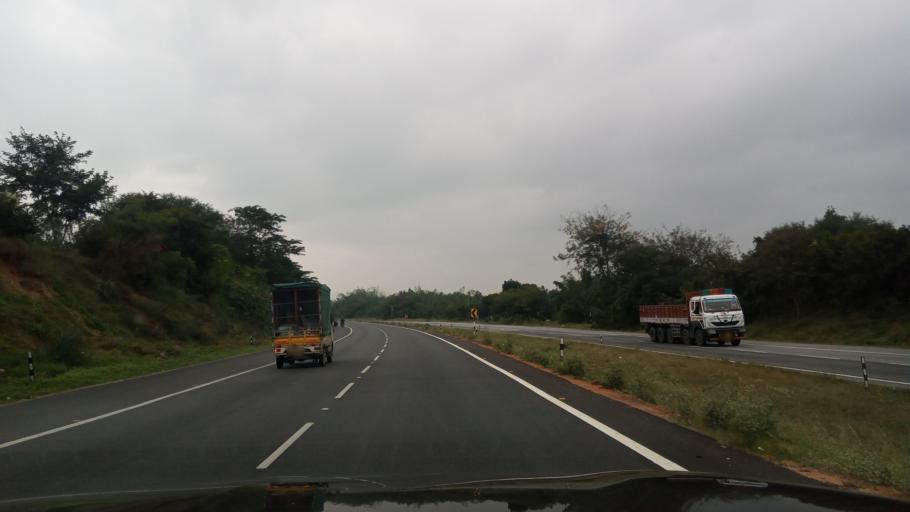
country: IN
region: Karnataka
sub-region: Bangalore Urban
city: Bangalore
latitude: 12.9843
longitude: 77.4709
